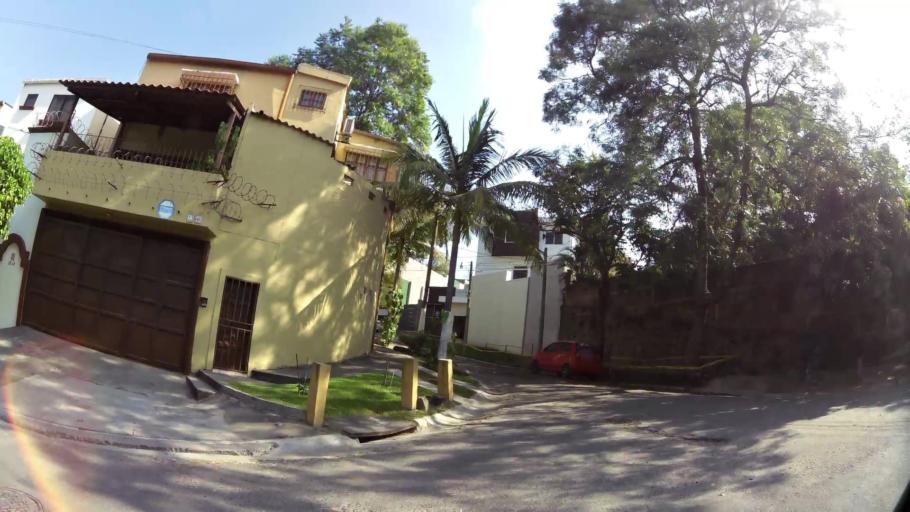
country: SV
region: La Libertad
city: Antiguo Cuscatlan
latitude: 13.6757
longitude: -89.2304
